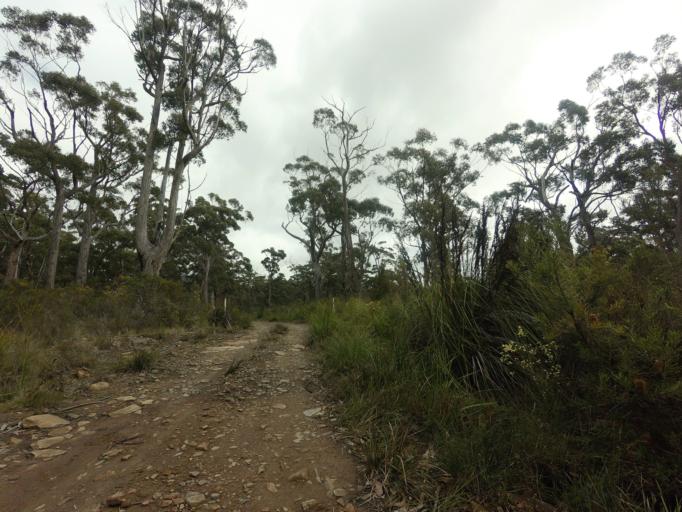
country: AU
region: Tasmania
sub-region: Huon Valley
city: Geeveston
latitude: -43.4614
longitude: 146.9143
